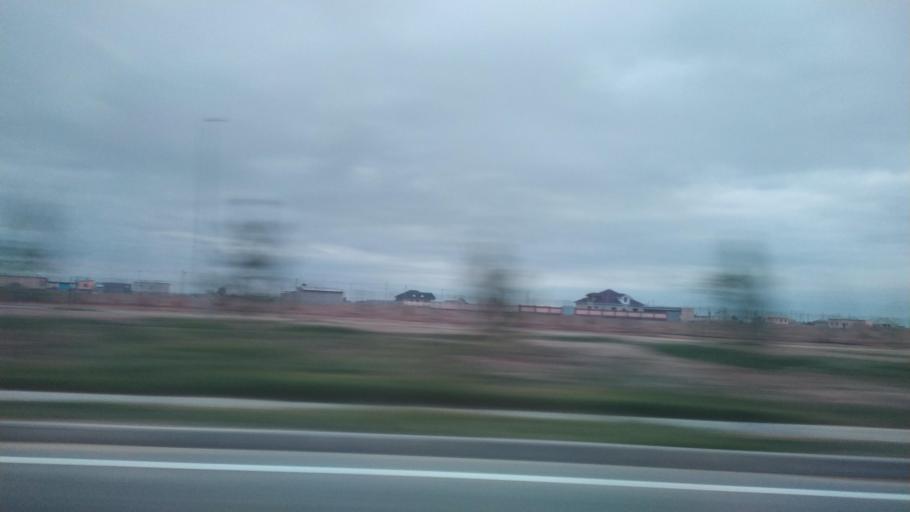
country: KZ
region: Ongtustik Qazaqstan
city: Turkestan
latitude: 43.2754
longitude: 68.4132
